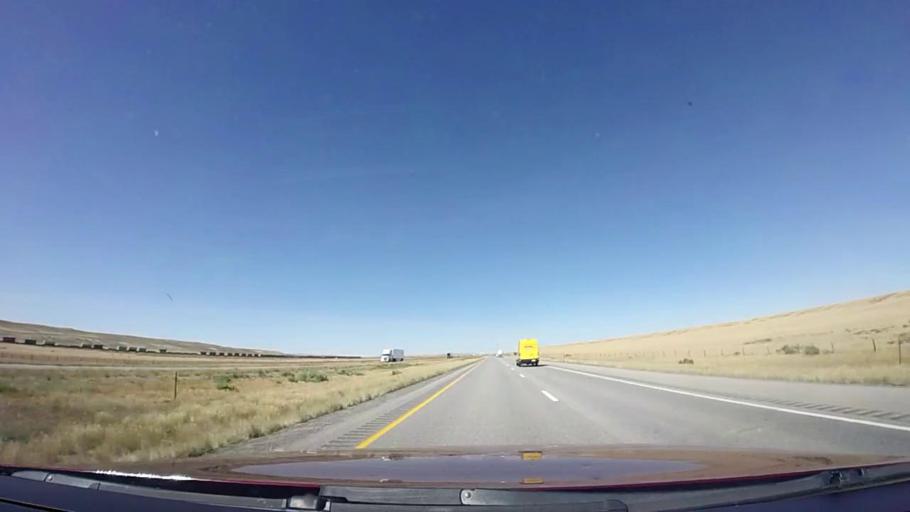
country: US
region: Wyoming
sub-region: Carbon County
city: Rawlins
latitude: 41.6582
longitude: -108.0876
